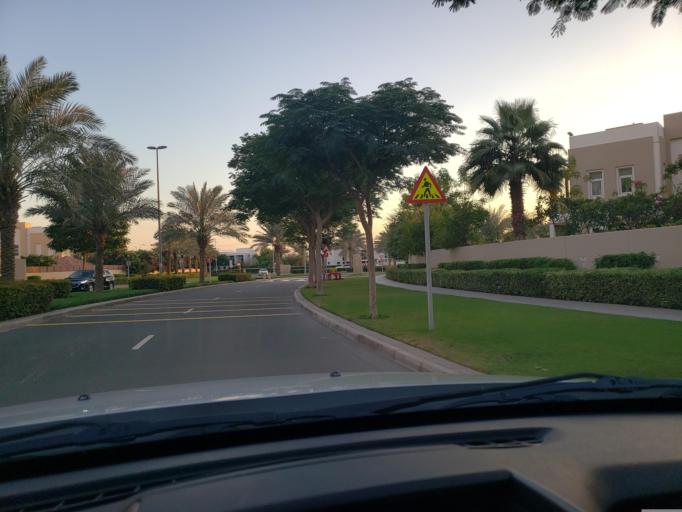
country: AE
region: Dubai
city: Dubai
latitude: 25.0213
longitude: 55.2741
